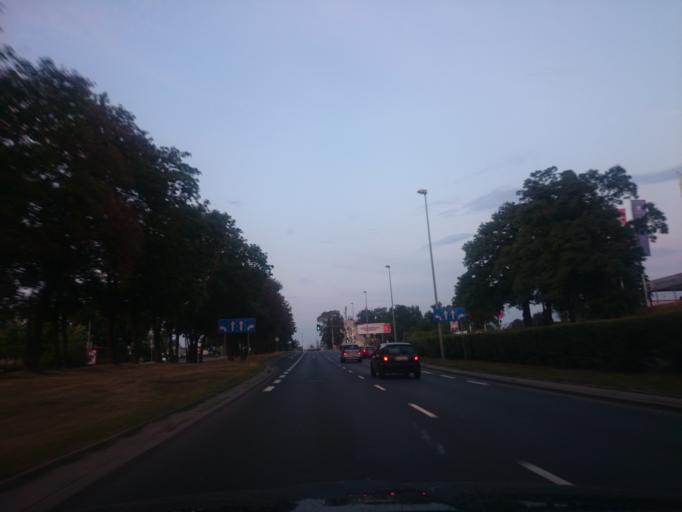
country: PL
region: West Pomeranian Voivodeship
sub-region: Szczecin
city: Szczecin
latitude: 53.4083
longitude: 14.5120
